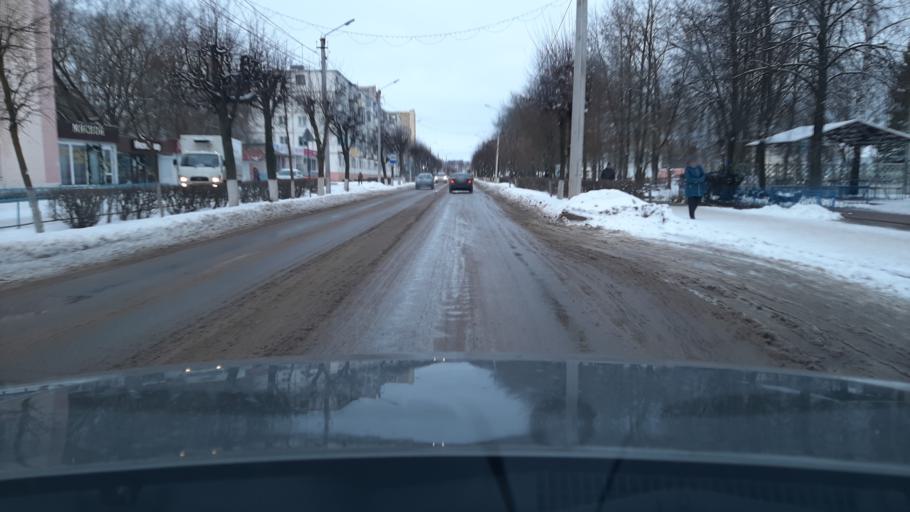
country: RU
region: Kostroma
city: Volgorechensk
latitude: 57.4398
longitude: 41.1564
